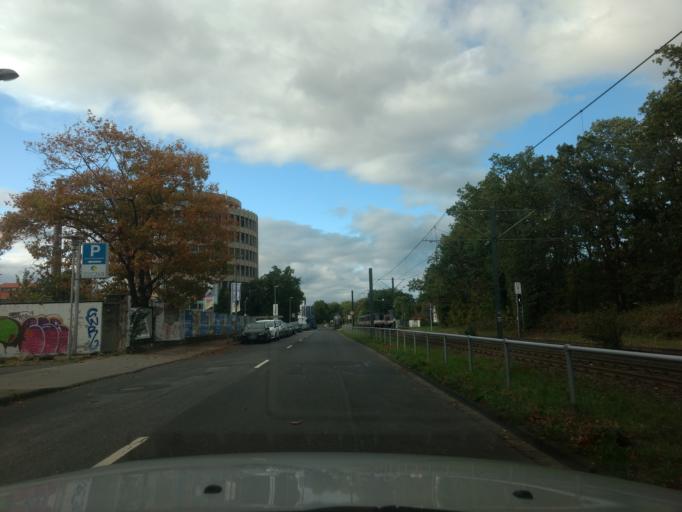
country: DE
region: North Rhine-Westphalia
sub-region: Regierungsbezirk Dusseldorf
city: Meerbusch
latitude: 51.2435
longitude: 6.7188
